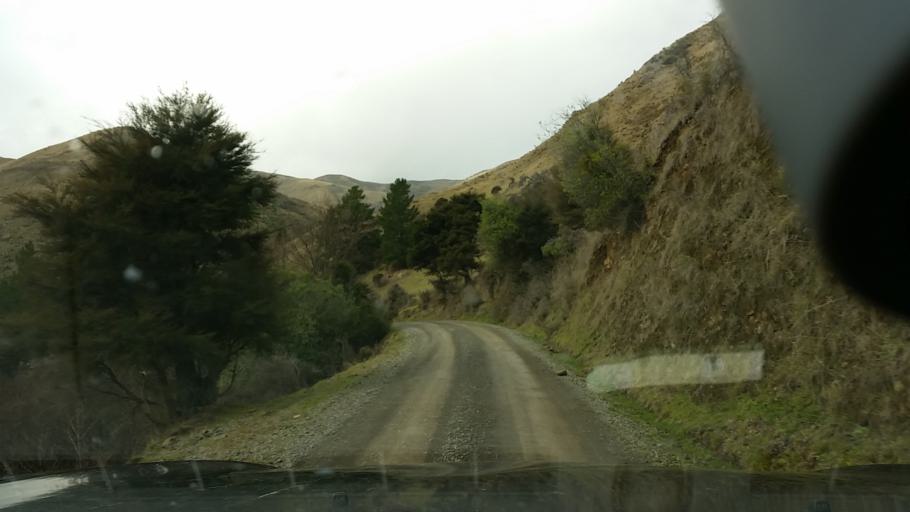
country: NZ
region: Tasman
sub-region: Tasman District
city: Richmond
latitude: -41.7310
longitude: 173.4624
